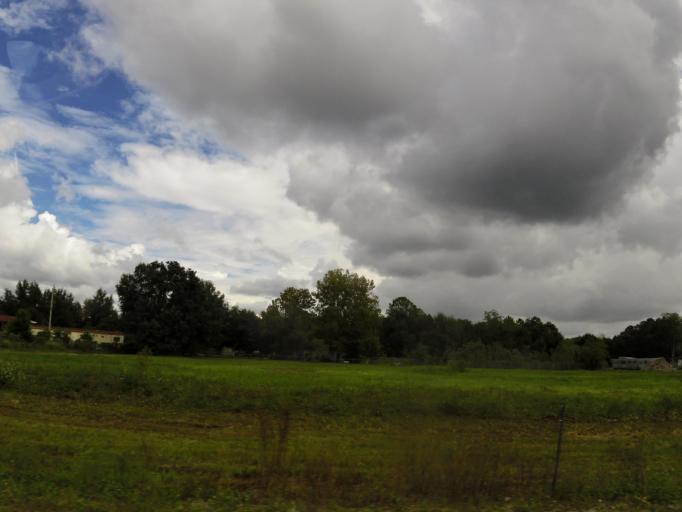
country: US
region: Florida
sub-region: Clay County
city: Middleburg
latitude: 30.1036
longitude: -81.9572
